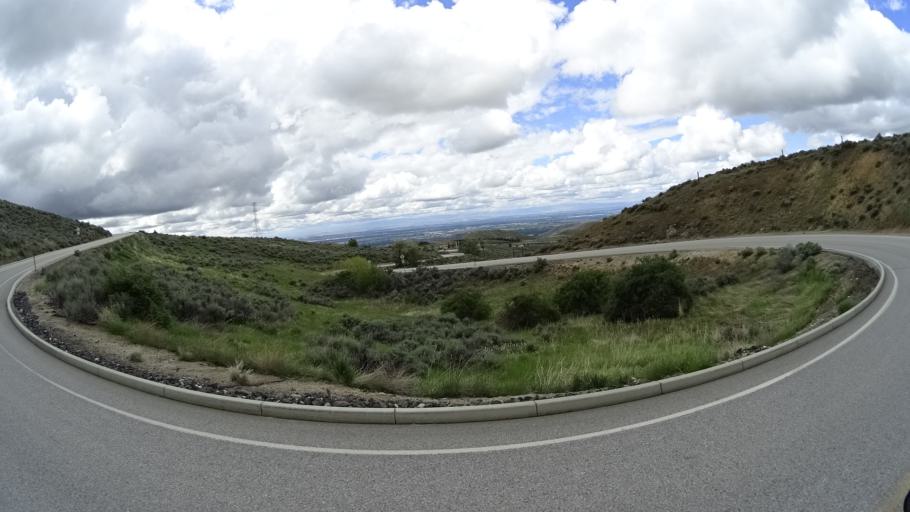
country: US
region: Idaho
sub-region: Ada County
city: Boise
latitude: 43.7014
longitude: -116.1669
